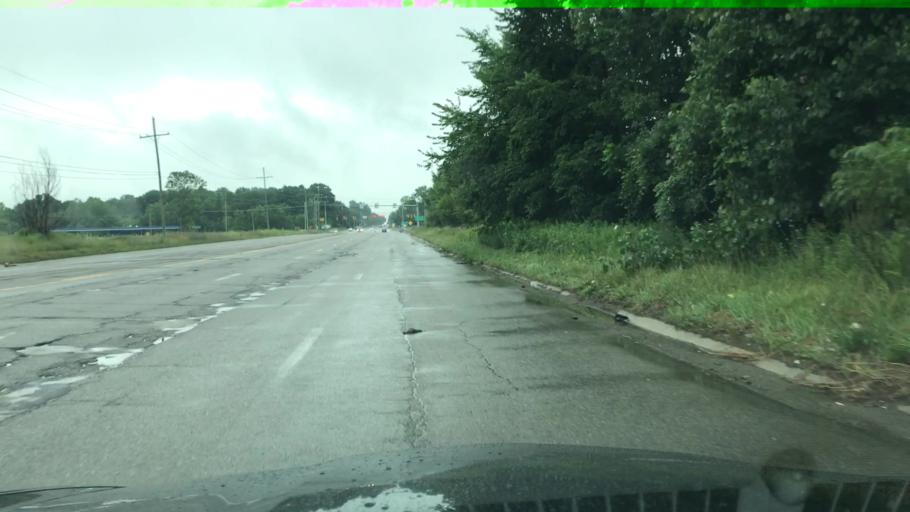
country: US
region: Michigan
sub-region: Oakland County
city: Auburn Hills
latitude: 42.7229
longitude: -83.2470
